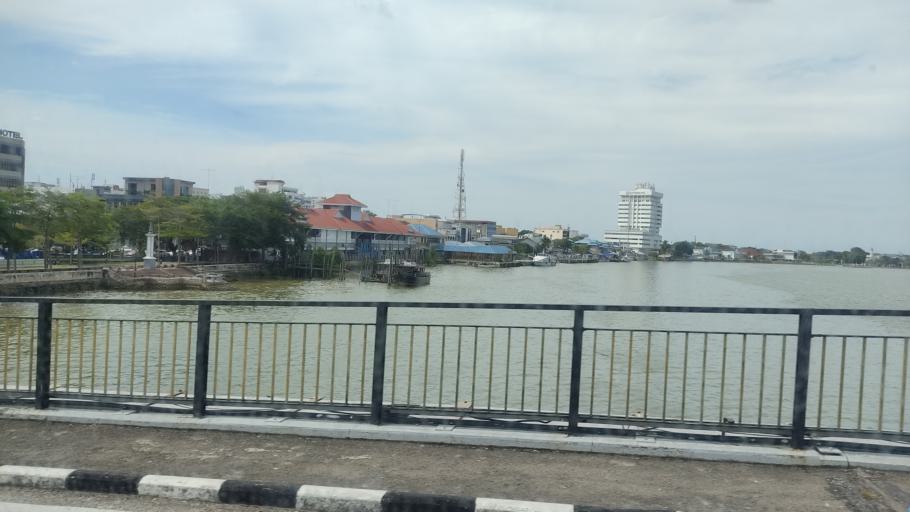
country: MY
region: Johor
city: Muar
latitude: 2.0498
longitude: 102.5679
